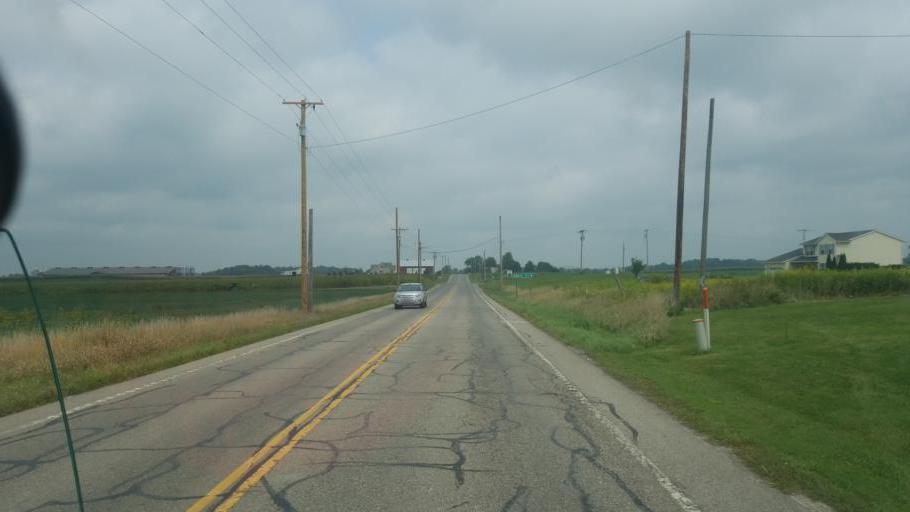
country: US
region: Ohio
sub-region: Huron County
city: Greenwich
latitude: 40.9300
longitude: -82.4964
